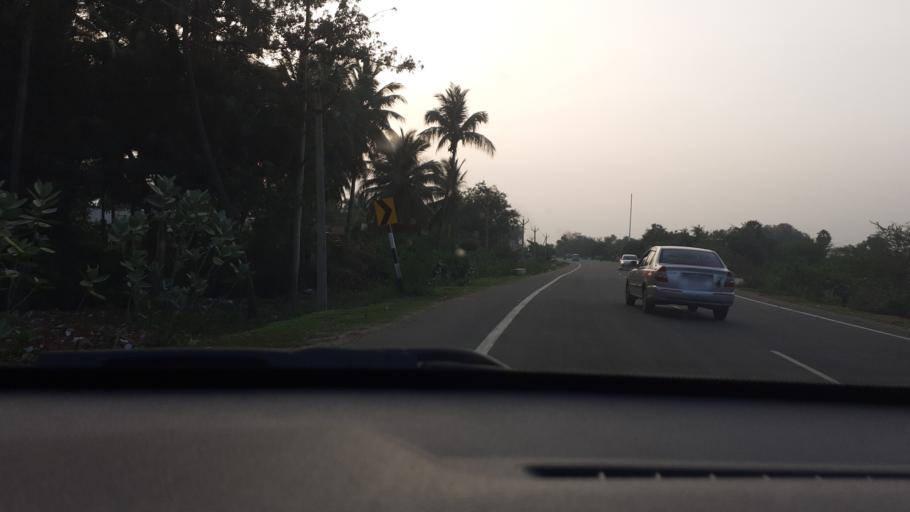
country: IN
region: Tamil Nadu
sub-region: Dindigul
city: Palani
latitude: 10.4320
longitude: 77.5162
